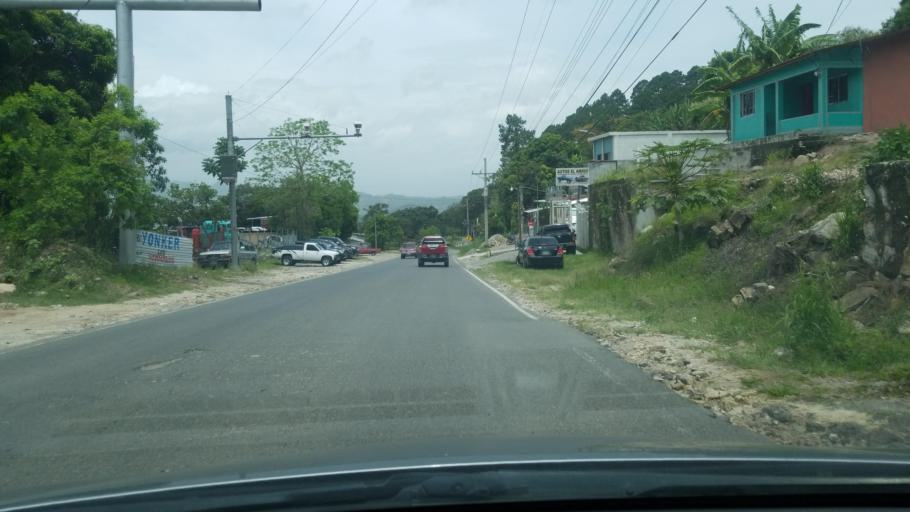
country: HN
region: Copan
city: Santa Rosa de Copan
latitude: 14.7541
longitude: -88.7779
